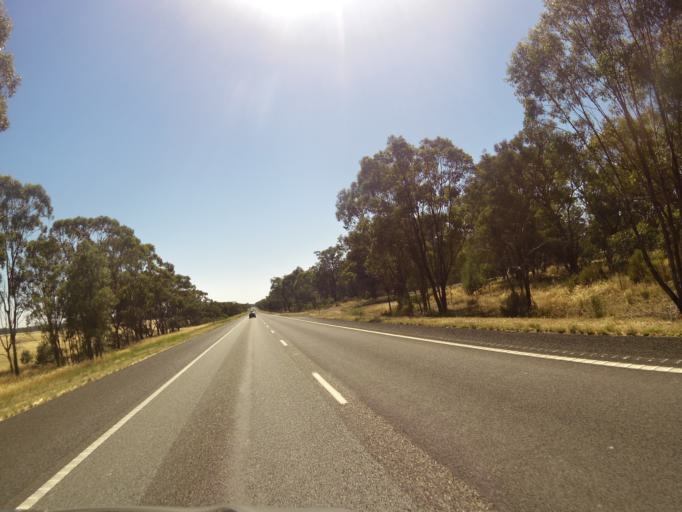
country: AU
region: Victoria
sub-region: Greater Shepparton
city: Shepparton
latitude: -36.8774
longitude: 145.2737
